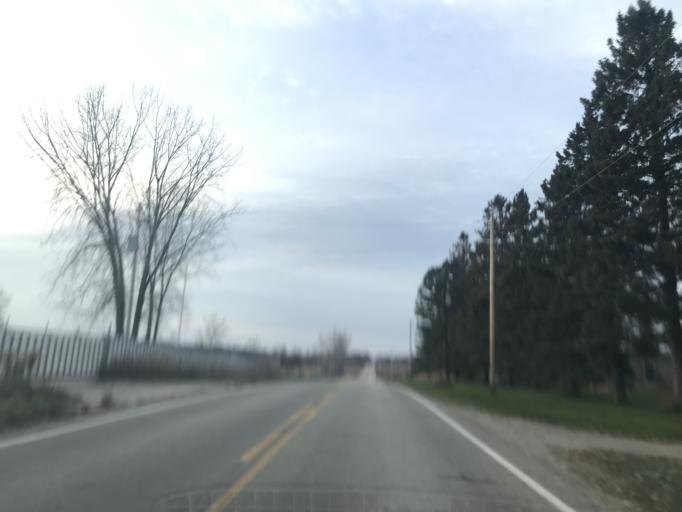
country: US
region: Wisconsin
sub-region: Marinette County
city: Peshtigo
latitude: 45.0994
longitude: -87.7994
